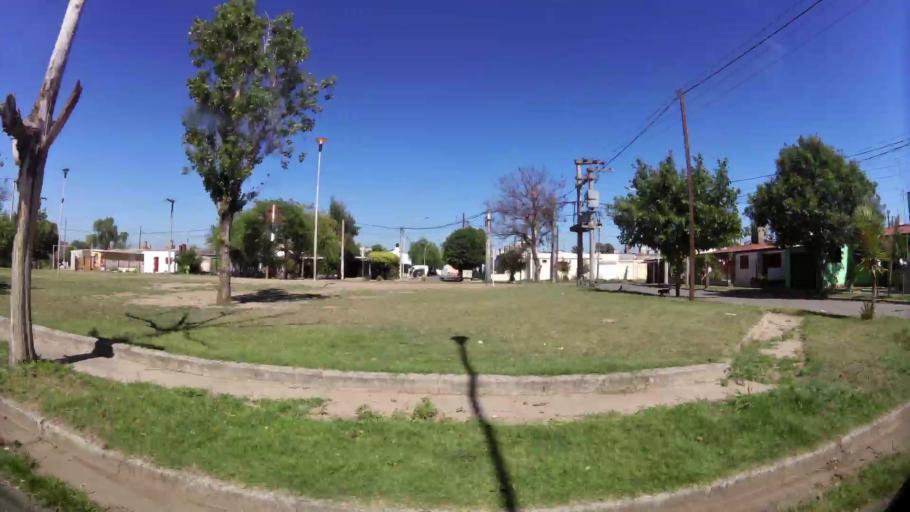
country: AR
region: Cordoba
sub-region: Departamento de Capital
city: Cordoba
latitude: -31.4432
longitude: -64.1362
